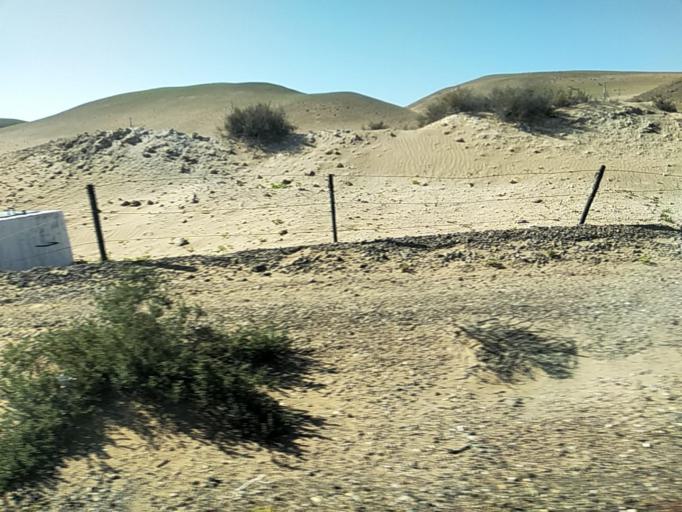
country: CL
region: Atacama
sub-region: Provincia de Copiapo
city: Copiapo
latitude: -27.3467
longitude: -70.7349
